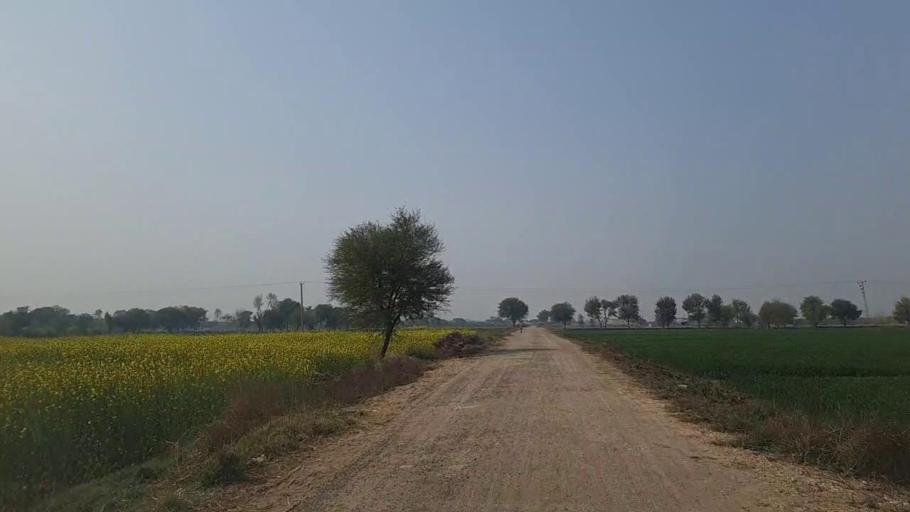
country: PK
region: Sindh
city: Daur
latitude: 26.4325
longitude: 68.4473
